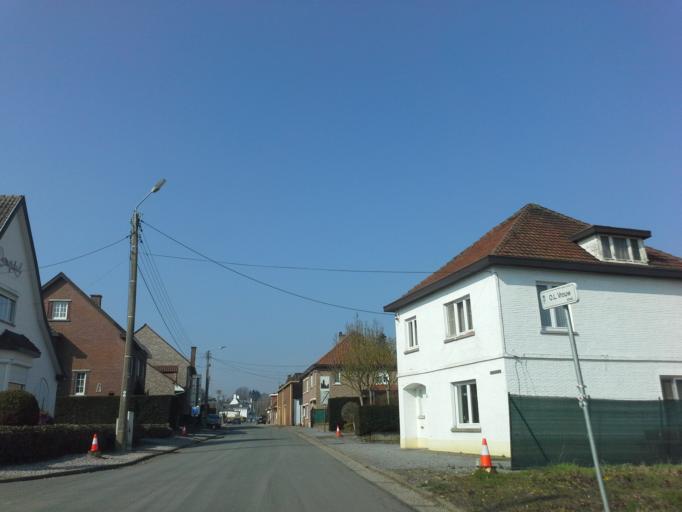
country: BE
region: Flanders
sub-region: Provincie Limburg
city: Hoeselt
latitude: 50.8454
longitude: 5.4933
